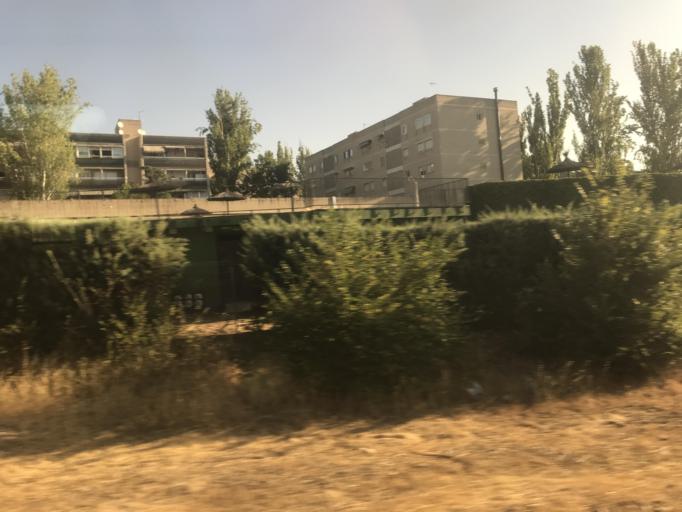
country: ES
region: Madrid
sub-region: Provincia de Madrid
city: Majadahonda
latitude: 40.4732
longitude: -3.8402
